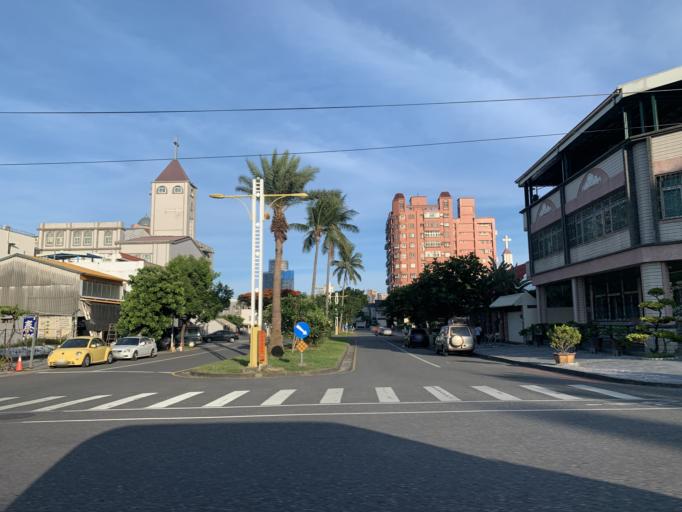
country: TW
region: Taiwan
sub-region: Hualien
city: Hualian
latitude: 23.9962
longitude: 121.6299
